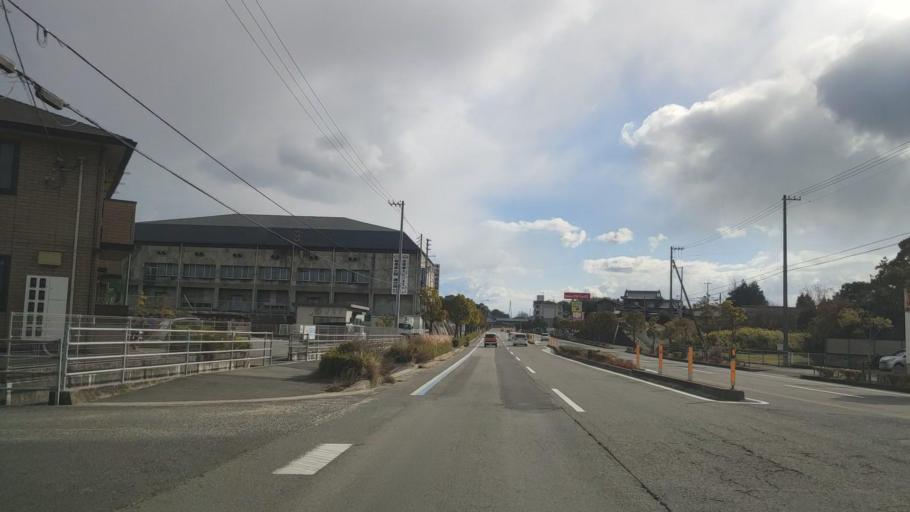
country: JP
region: Ehime
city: Hojo
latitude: 34.0601
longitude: 132.9667
